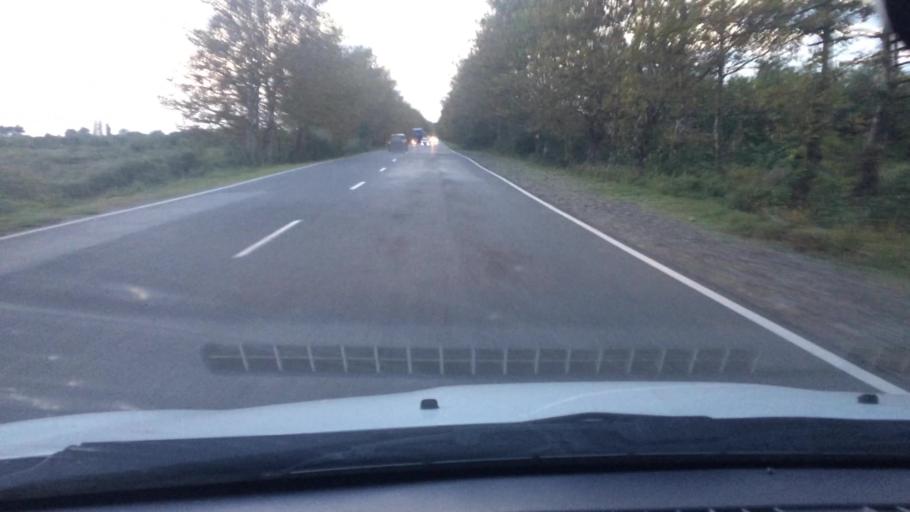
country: GE
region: Guria
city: Urek'i
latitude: 42.0167
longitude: 41.7683
